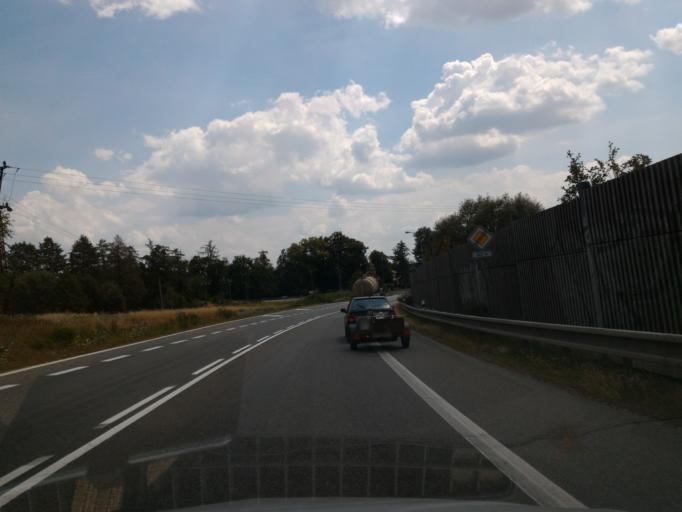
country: CZ
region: Vysocina
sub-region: Okres Havlickuv Brod
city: Havlickuv Brod
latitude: 49.6082
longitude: 15.6021
